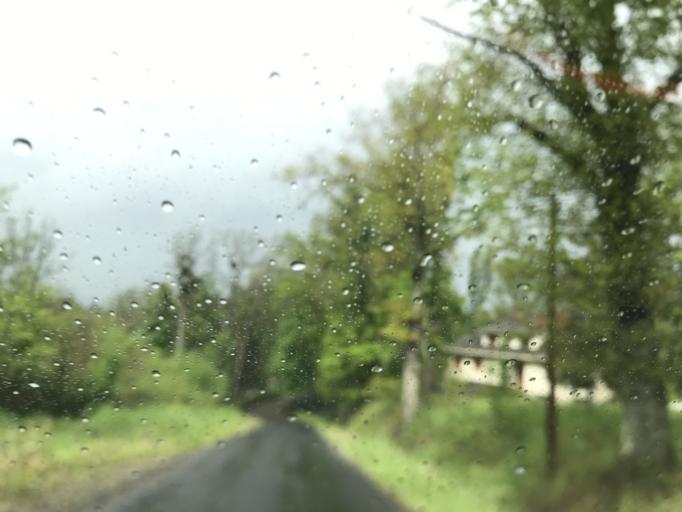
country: FR
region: Auvergne
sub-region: Departement du Puy-de-Dome
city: Courpiere
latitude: 45.7481
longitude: 3.5278
